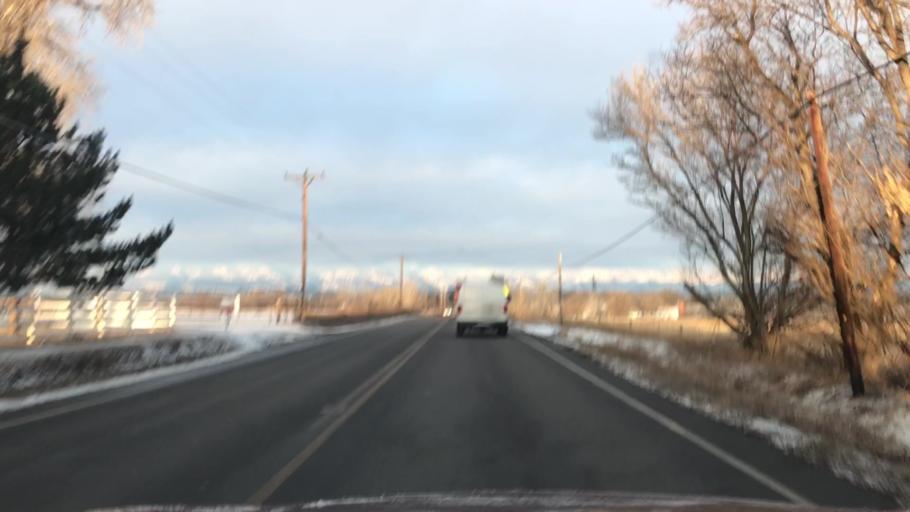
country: US
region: Colorado
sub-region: Boulder County
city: Louisville
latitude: 40.0147
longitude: -105.1618
